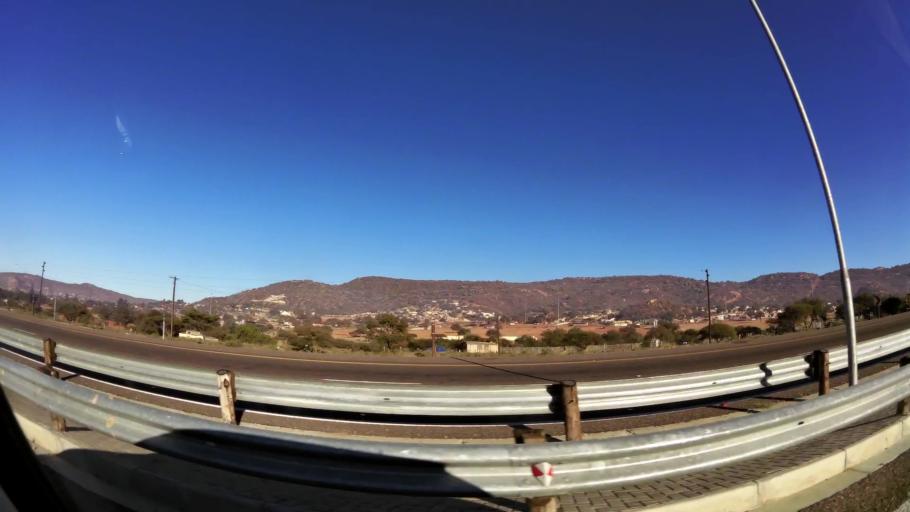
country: ZA
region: Limpopo
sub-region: Capricorn District Municipality
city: Mankoeng
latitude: -23.9391
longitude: 29.7948
